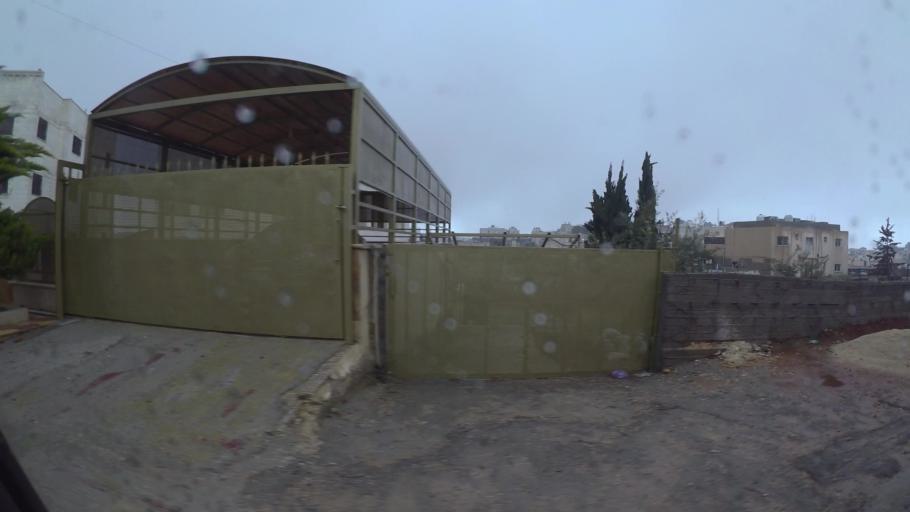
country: JO
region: Amman
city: Al Jubayhah
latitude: 32.0202
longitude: 35.8366
